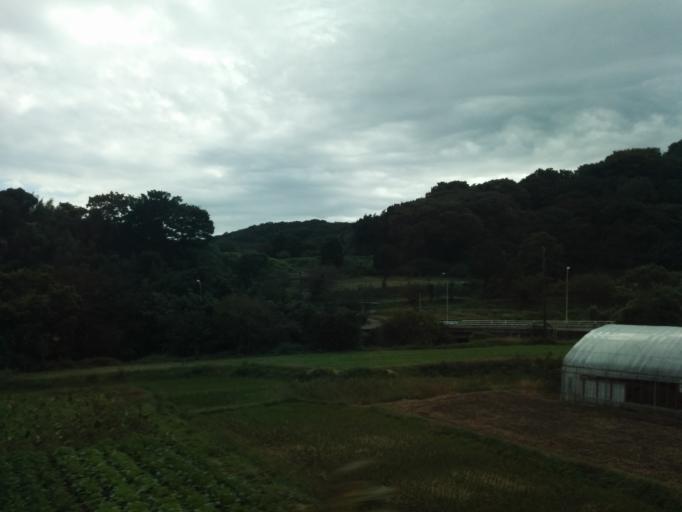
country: JP
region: Kanagawa
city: Oiso
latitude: 35.3294
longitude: 139.2944
